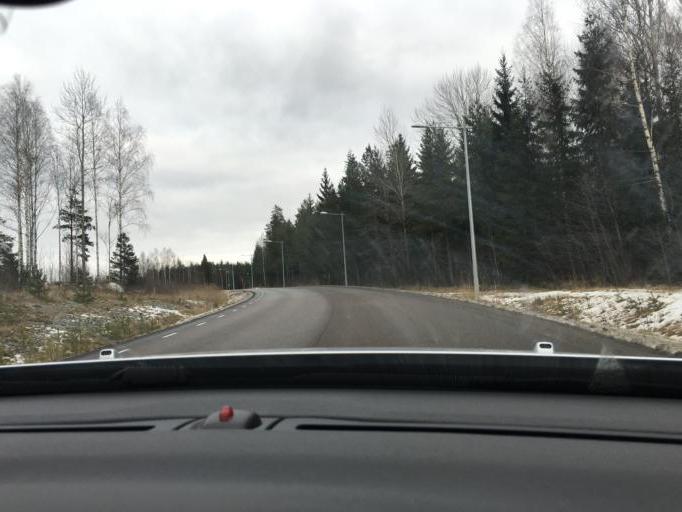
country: SE
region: Soedermanland
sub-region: Katrineholms Kommun
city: Katrineholm
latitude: 58.9946
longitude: 16.2446
